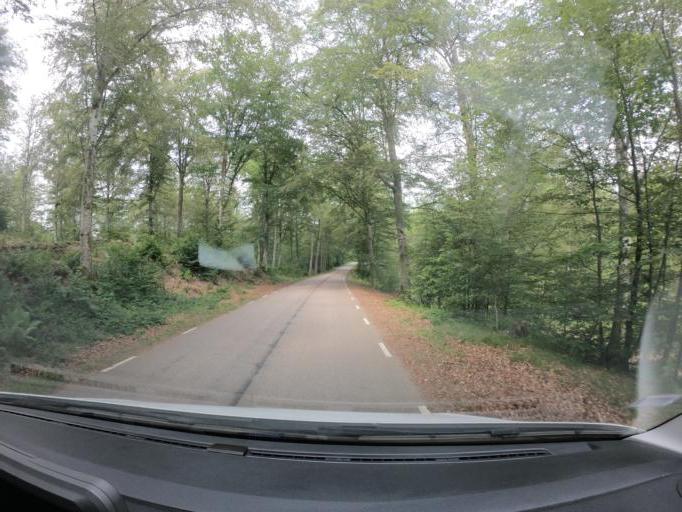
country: SE
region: Skane
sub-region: Hassleholms Kommun
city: Bjarnum
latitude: 56.2744
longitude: 13.7118
